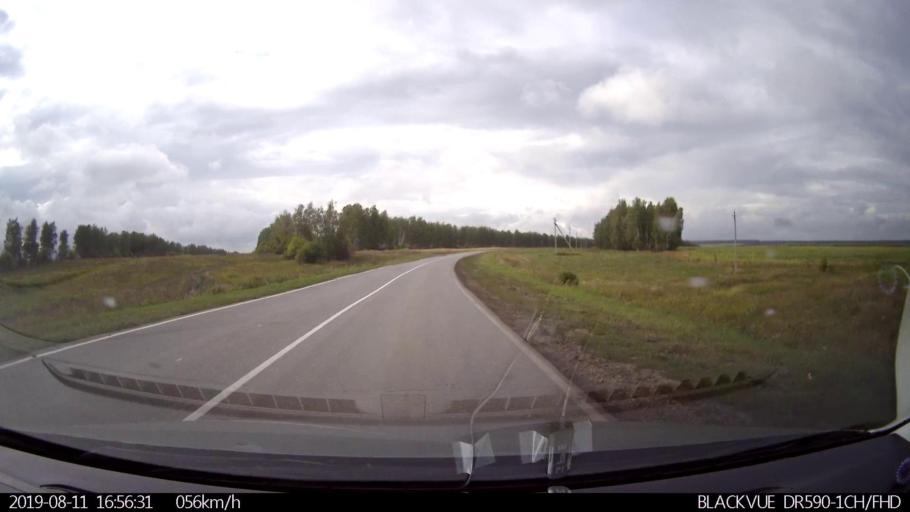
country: RU
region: Ulyanovsk
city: Mayna
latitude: 54.2882
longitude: 47.6531
